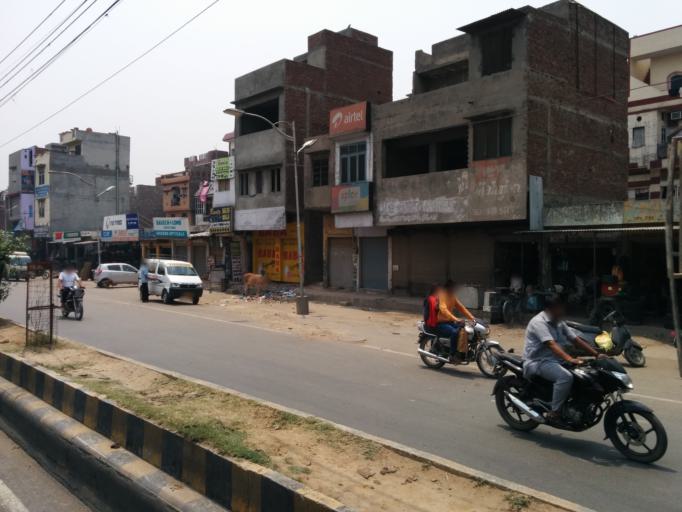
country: IN
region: Punjab
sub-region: Amritsar
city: Amritsar
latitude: 31.6293
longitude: 74.8815
